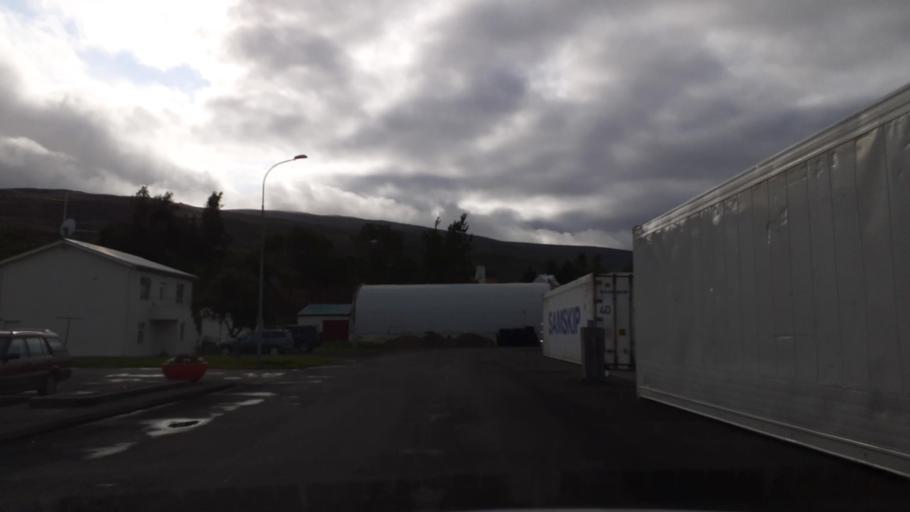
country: IS
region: Northeast
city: Akureyri
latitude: 65.7433
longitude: -18.0863
